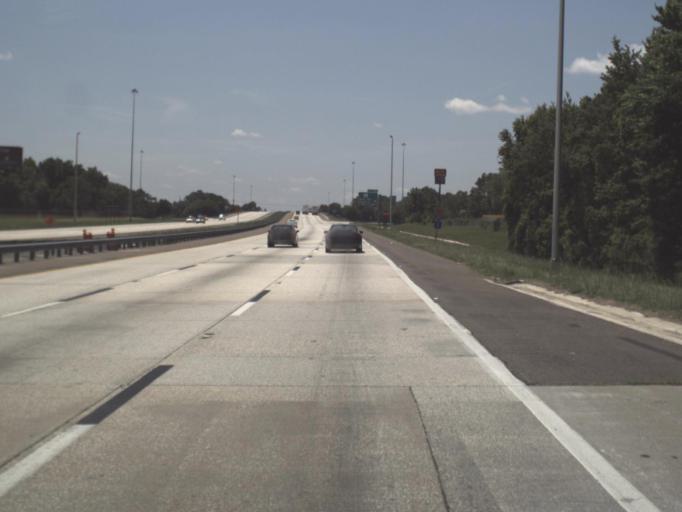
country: US
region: Florida
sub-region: Duval County
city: Jacksonville
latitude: 30.4364
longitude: -81.6559
